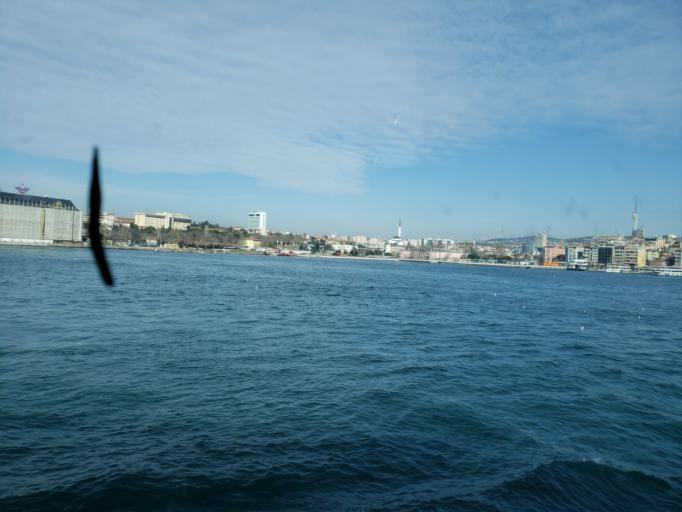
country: TR
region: Istanbul
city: UEskuedar
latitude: 40.9923
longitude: 29.0195
